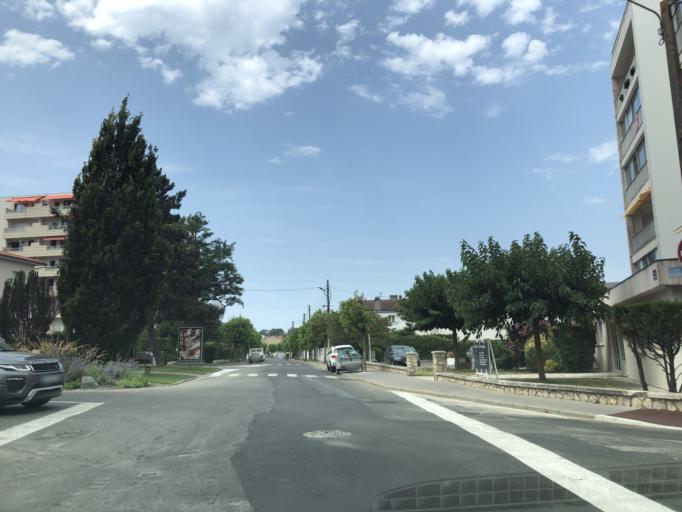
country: FR
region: Poitou-Charentes
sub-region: Departement de la Charente-Maritime
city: Royan
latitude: 45.6242
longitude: -1.0367
